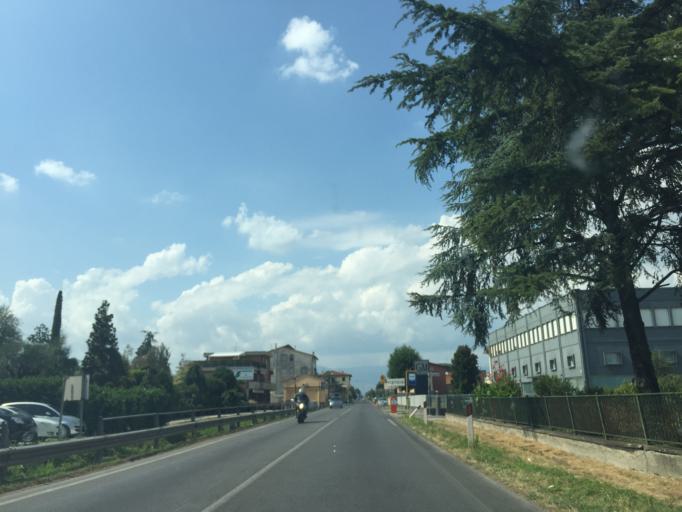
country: IT
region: Tuscany
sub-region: Provincia di Pistoia
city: Barba
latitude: 43.8826
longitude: 10.9715
